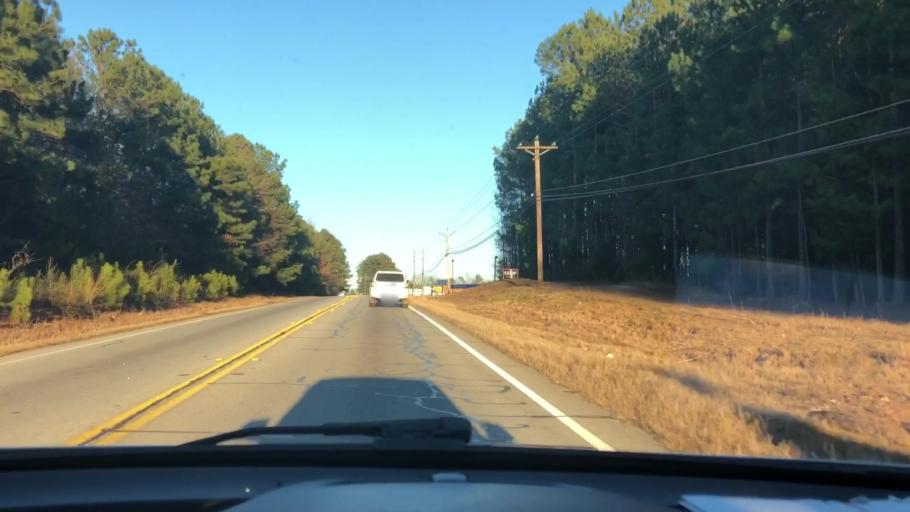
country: US
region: Georgia
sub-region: Walton County
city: Loganville
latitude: 33.7861
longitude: -83.9607
